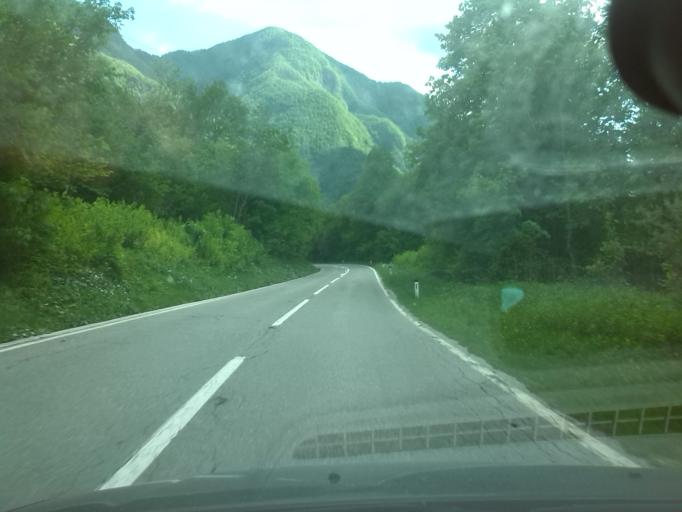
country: IT
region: Friuli Venezia Giulia
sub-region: Provincia di Udine
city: Pulfero
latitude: 46.2261
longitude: 13.5004
